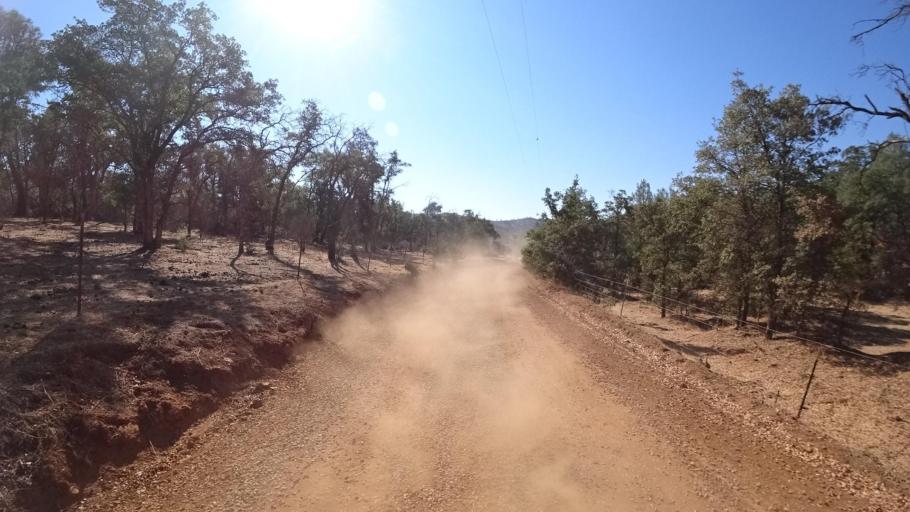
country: US
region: California
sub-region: Mariposa County
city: Mariposa
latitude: 37.6199
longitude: -120.2367
